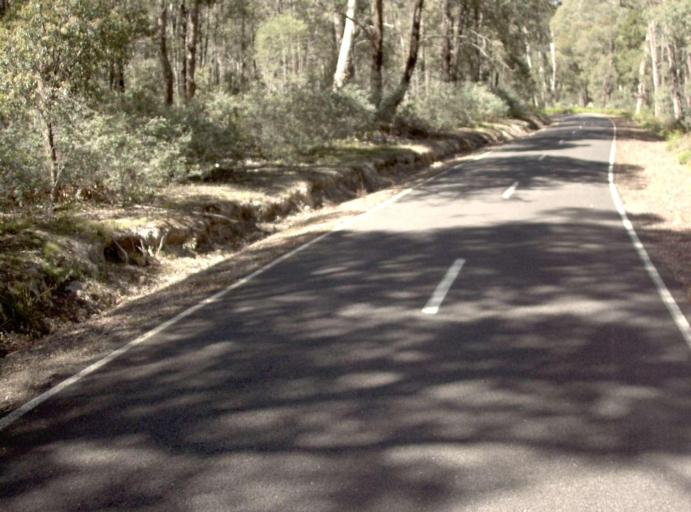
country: AU
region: New South Wales
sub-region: Bombala
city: Bombala
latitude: -37.1332
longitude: 148.7421
